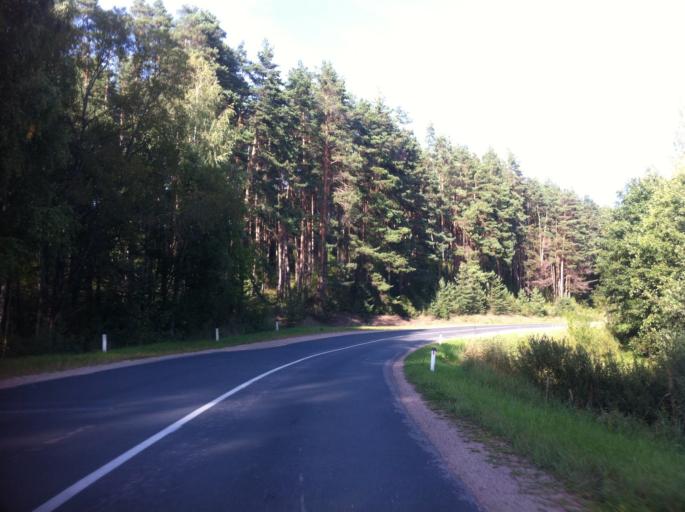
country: RU
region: Pskov
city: Izborsk
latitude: 57.8353
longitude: 27.9212
